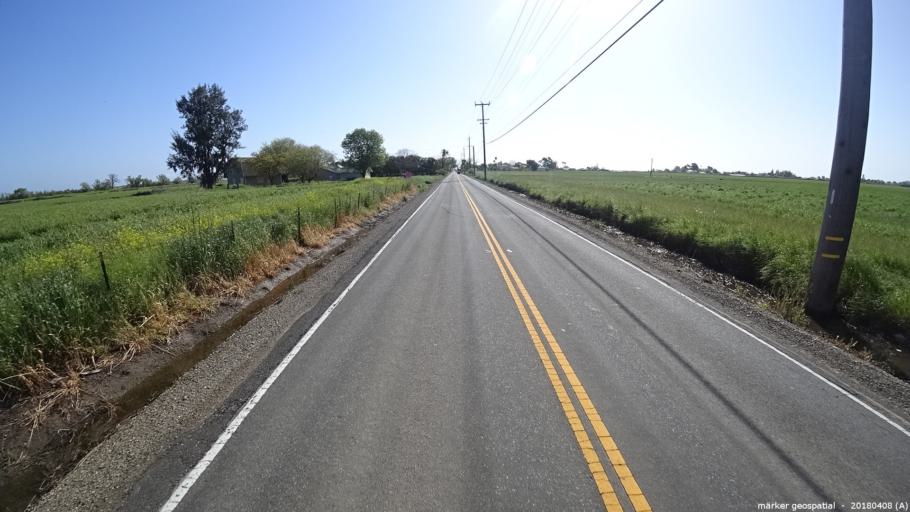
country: US
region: California
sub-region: Sacramento County
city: Laguna
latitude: 38.3723
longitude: -121.4127
